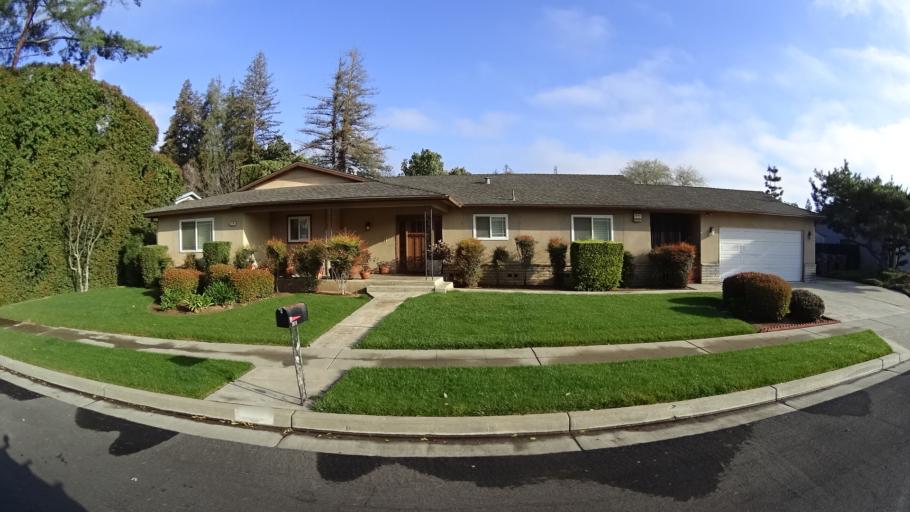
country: US
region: California
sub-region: Fresno County
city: Fresno
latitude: 36.8274
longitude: -119.8280
